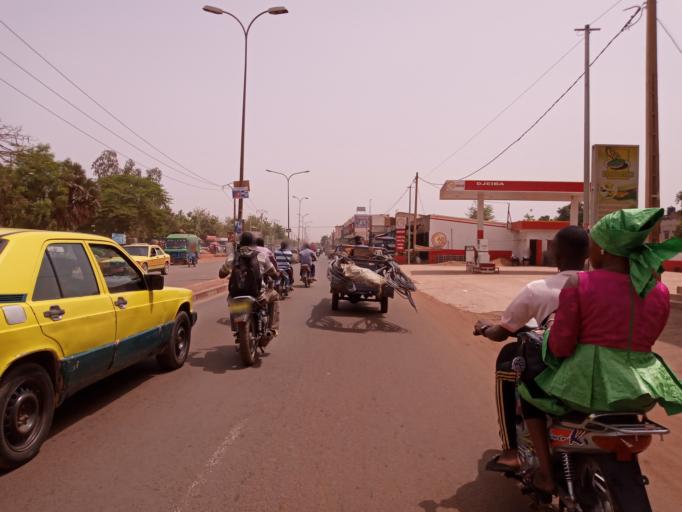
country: ML
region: Bamako
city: Bamako
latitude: 12.6665
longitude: -7.9305
